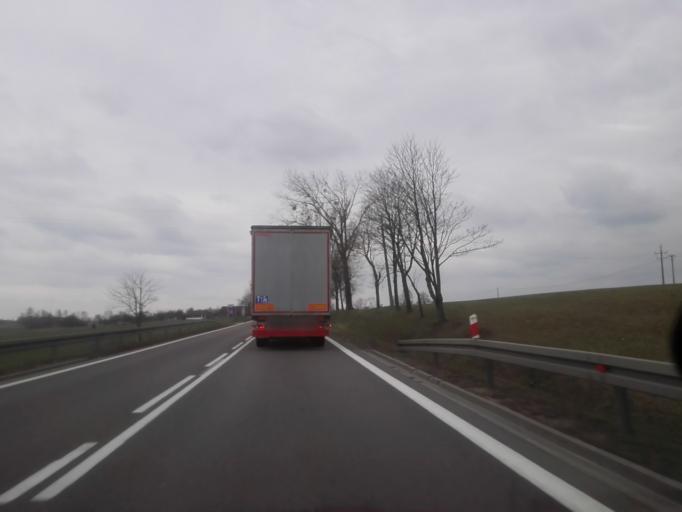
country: PL
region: Podlasie
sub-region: Powiat augustowski
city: Augustow
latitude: 53.7951
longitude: 22.8741
